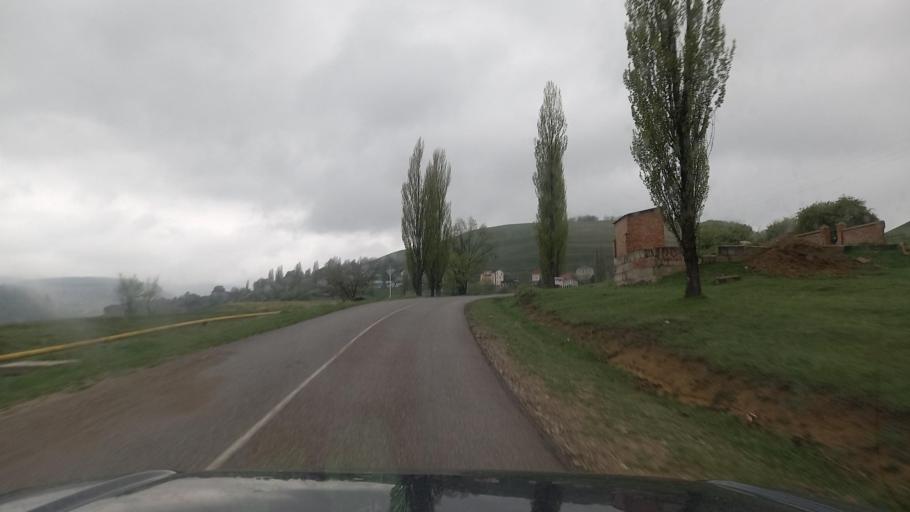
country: RU
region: Stavropol'skiy
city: Nezhinskiy
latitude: 43.8737
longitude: 42.6722
